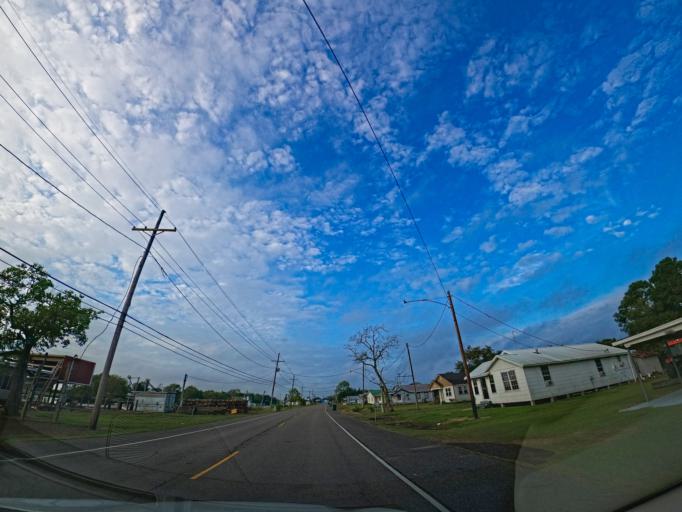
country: US
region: Louisiana
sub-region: Terrebonne Parish
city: Chauvin
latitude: 29.3941
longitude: -90.6133
